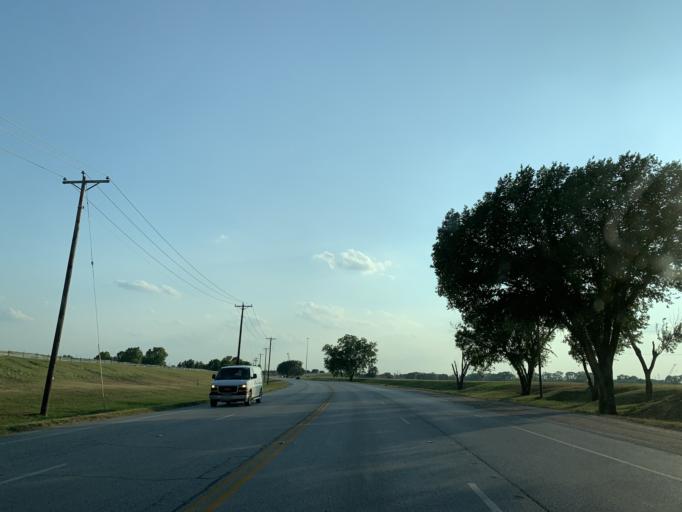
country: US
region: Texas
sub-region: Tarrant County
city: Richland Hills
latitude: 32.8017
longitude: -97.2043
